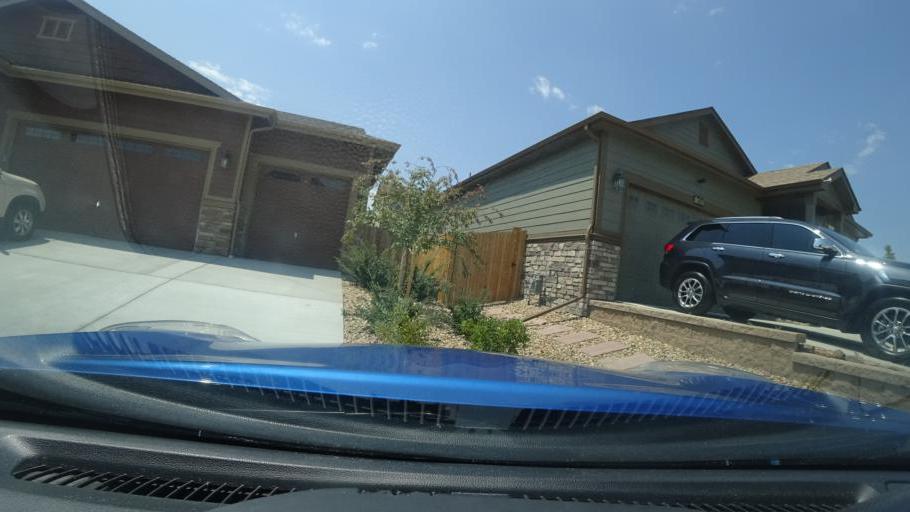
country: US
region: Colorado
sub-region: Adams County
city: Aurora
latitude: 39.6813
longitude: -104.7653
